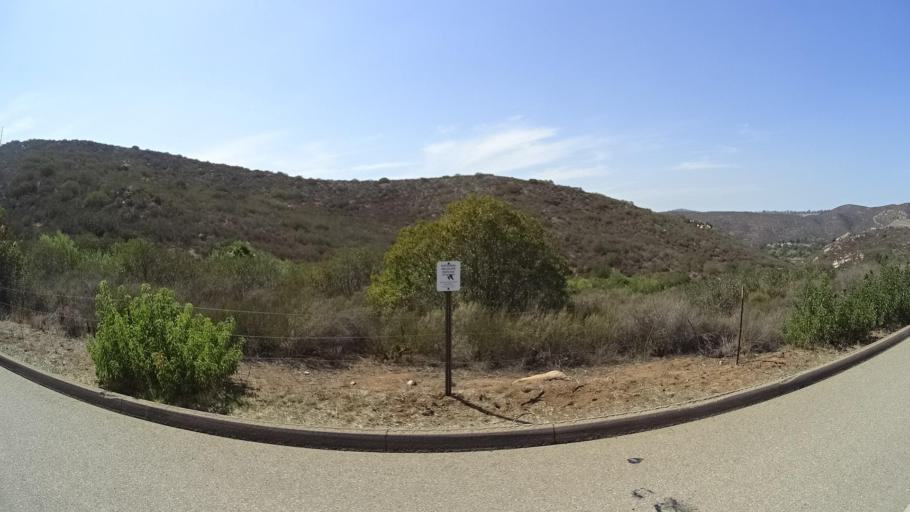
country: US
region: California
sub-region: San Diego County
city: Rancho San Diego
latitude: 32.7248
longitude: -116.9333
